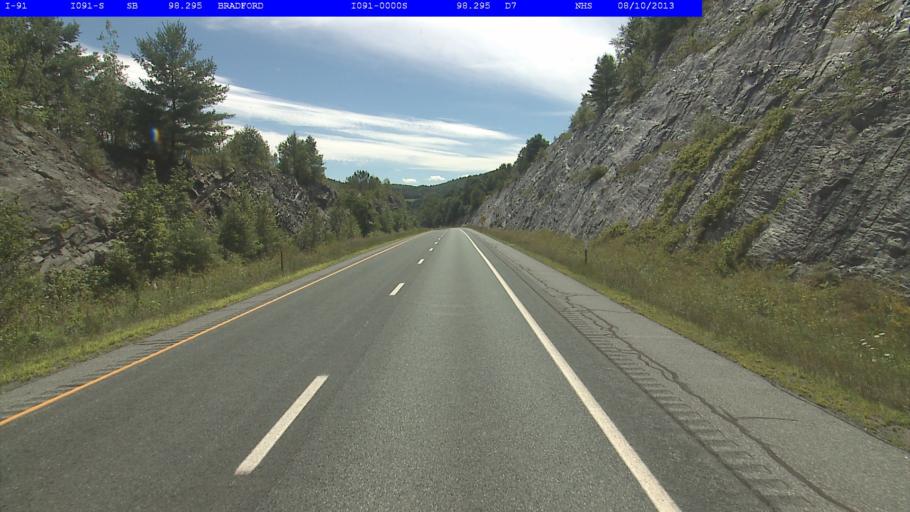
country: US
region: New Hampshire
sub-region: Grafton County
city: Haverhill
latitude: 43.9925
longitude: -72.1346
